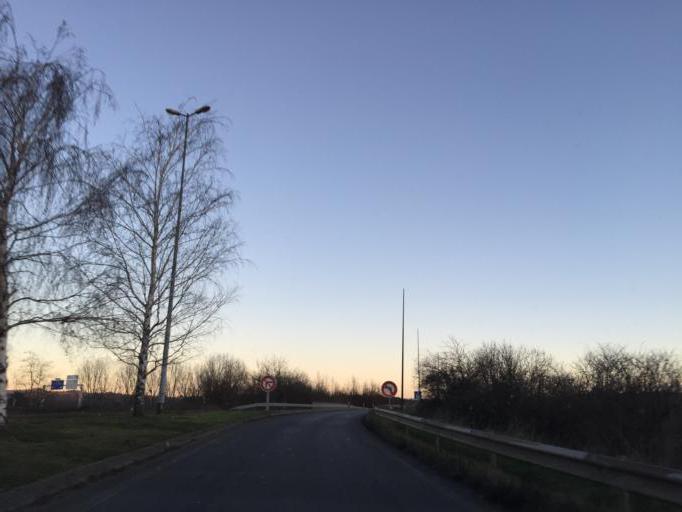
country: FR
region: Rhone-Alpes
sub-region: Departement de la Loire
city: Andrezieux-Boutheon
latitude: 45.5297
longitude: 4.2831
